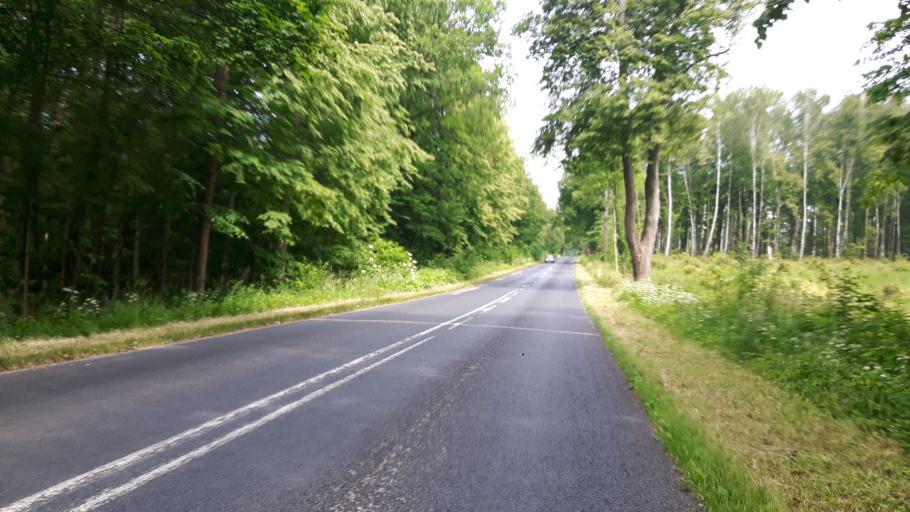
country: PL
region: Warmian-Masurian Voivodeship
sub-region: Powiat braniewski
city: Frombork
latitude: 54.3616
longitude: 19.7350
